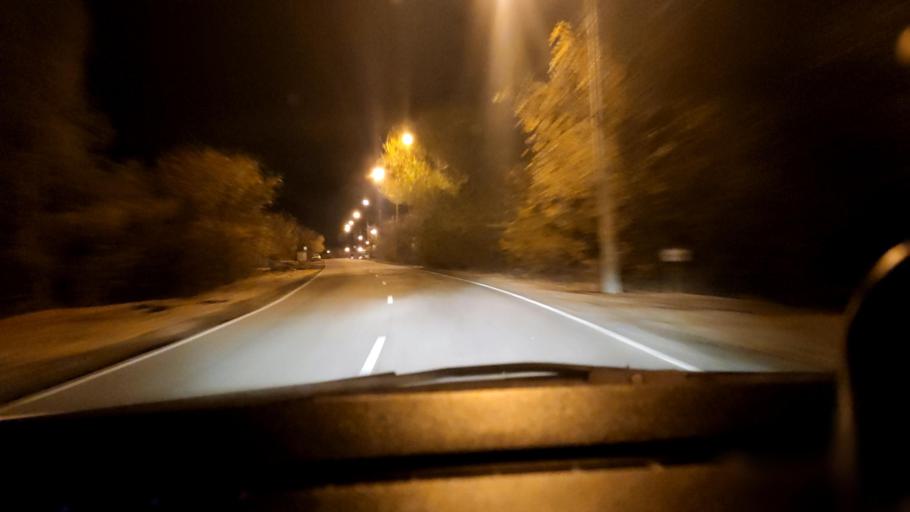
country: RU
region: Voronezj
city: Shilovo
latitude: 51.6054
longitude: 39.0392
